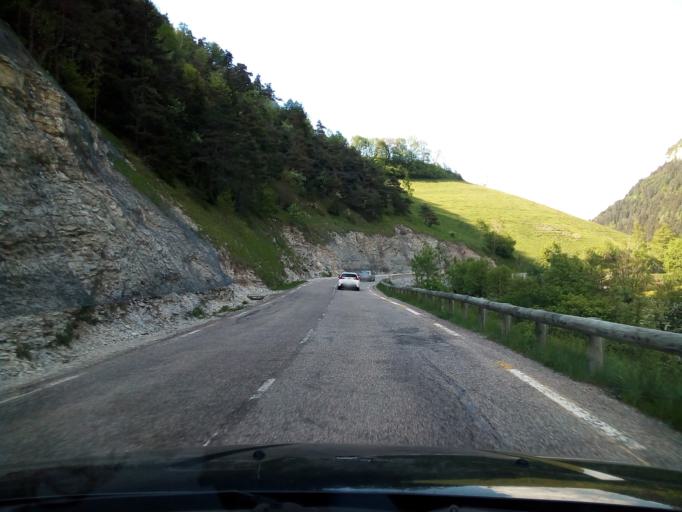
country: FR
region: Rhone-Alpes
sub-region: Departement de l'Isere
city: Lans-en-Vercors
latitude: 45.1730
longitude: 5.6148
